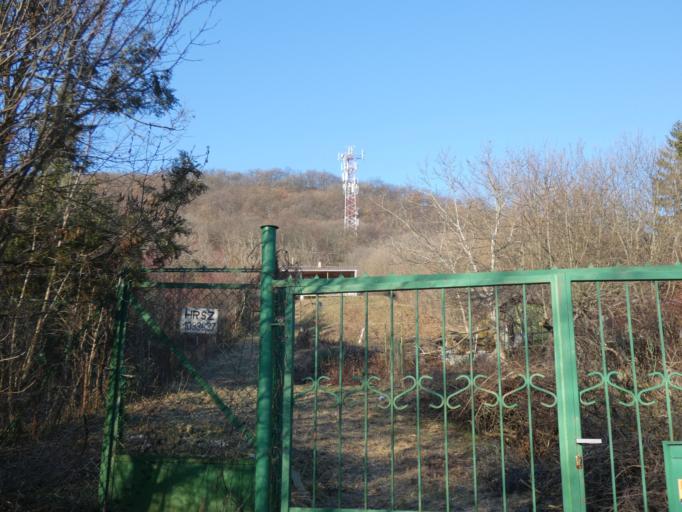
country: HU
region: Pest
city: Nagymaros
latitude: 47.7843
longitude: 18.9496
